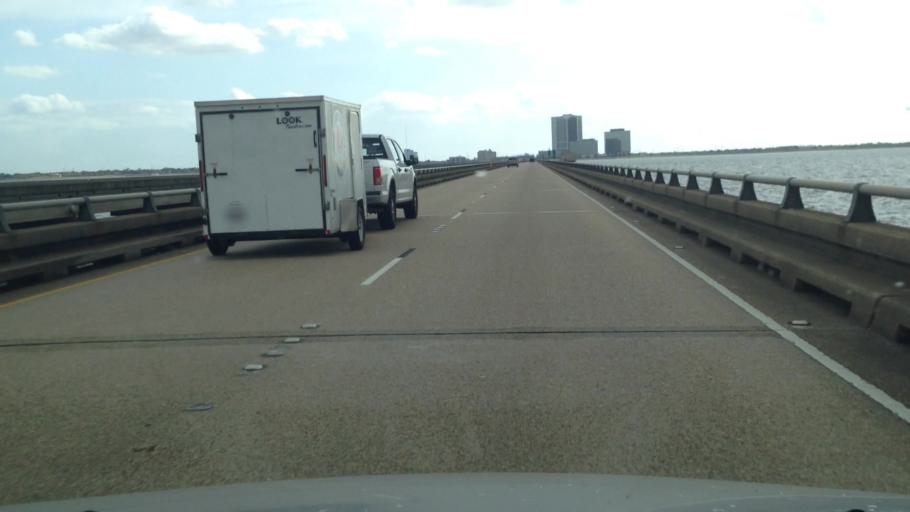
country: US
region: Louisiana
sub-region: Jefferson Parish
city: Metairie
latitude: 30.0417
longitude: -90.1506
